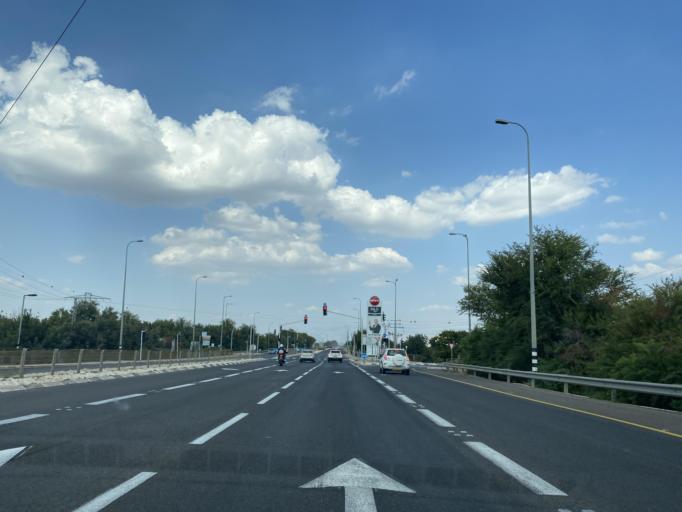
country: IL
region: Northern District
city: Rosh Pinna
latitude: 32.9896
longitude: 35.5610
